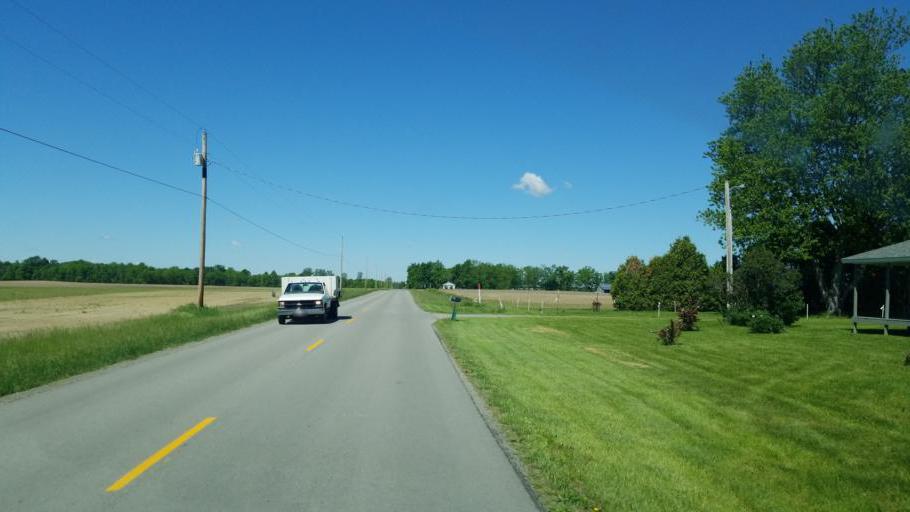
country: US
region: Ohio
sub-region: Logan County
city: Russells Point
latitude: 40.4252
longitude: -83.8438
